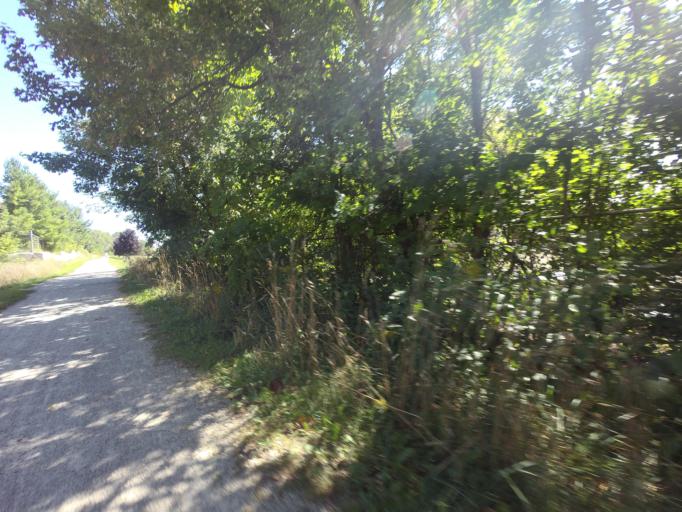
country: CA
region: Ontario
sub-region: Wellington County
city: Guelph
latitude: 43.6917
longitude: -80.4166
